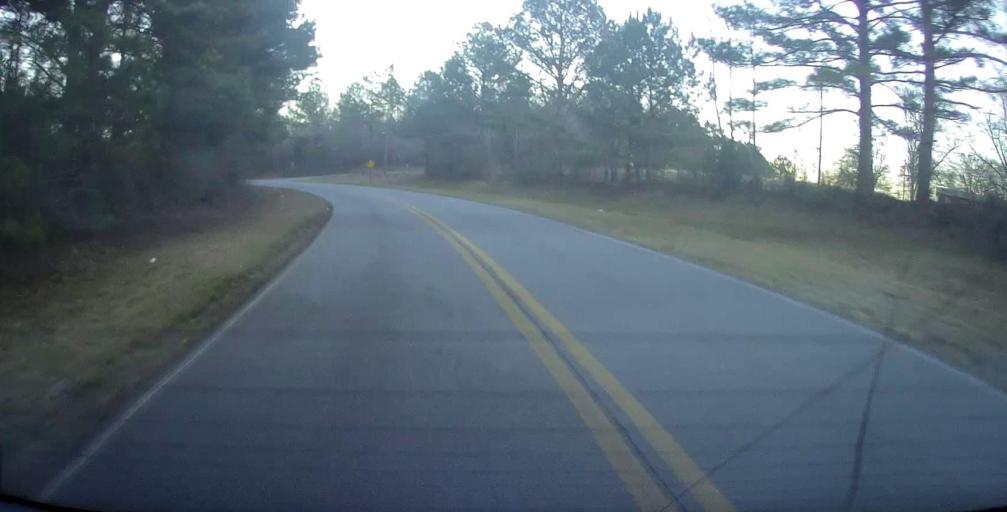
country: US
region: Georgia
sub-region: Troup County
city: La Grange
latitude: 33.0497
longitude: -84.9708
